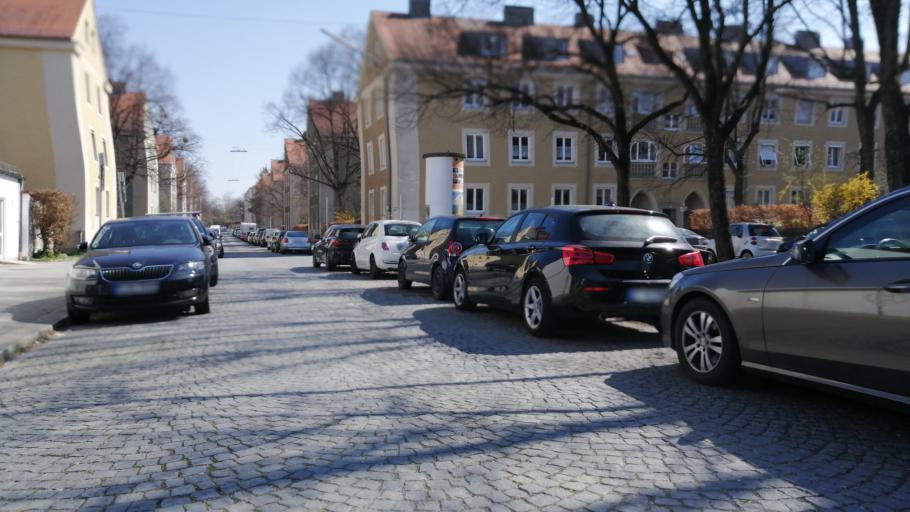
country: DE
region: Bavaria
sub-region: Upper Bavaria
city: Bogenhausen
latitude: 48.1790
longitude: 11.5980
